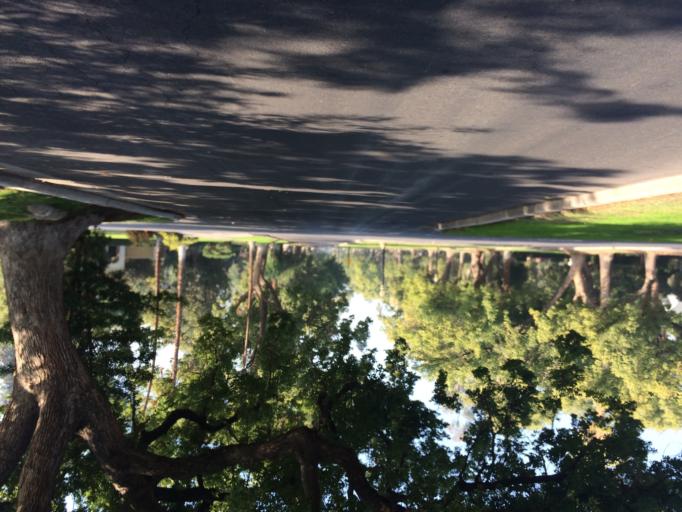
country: US
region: California
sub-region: Fresno County
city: Fresno
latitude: 36.7393
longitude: -119.7664
